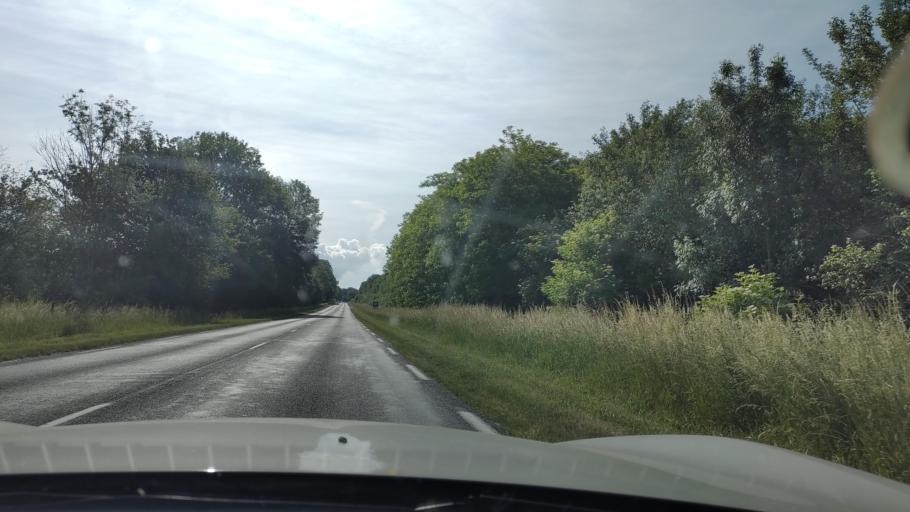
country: FR
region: Ile-de-France
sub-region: Departement de Seine-et-Marne
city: Sourdun
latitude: 48.5308
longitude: 3.3894
